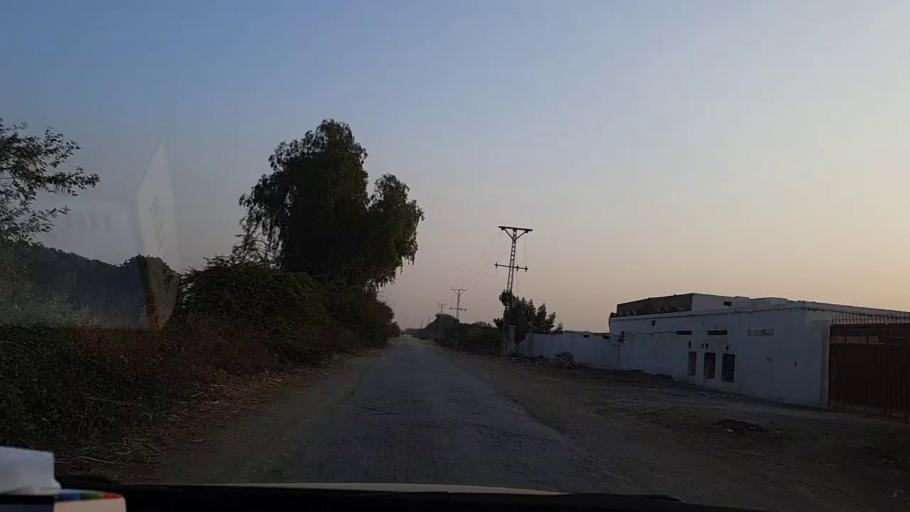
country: PK
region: Sindh
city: Tando Ghulam Ali
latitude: 25.1732
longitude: 68.9489
